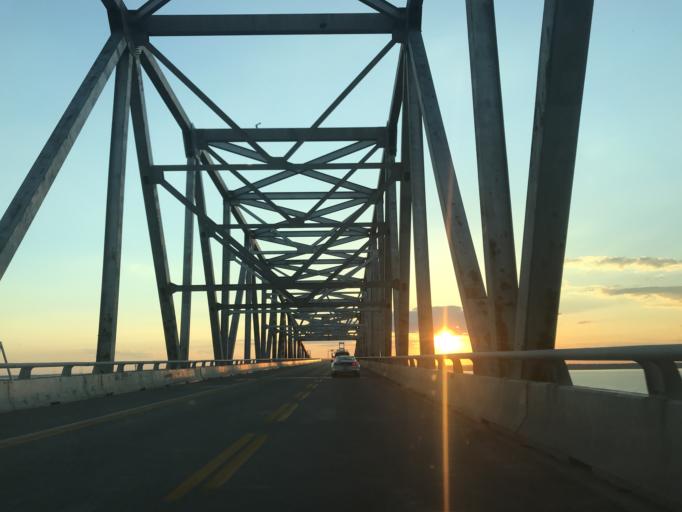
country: US
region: Maryland
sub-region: Queen Anne's County
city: Stevensville
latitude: 38.9890
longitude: -76.3578
